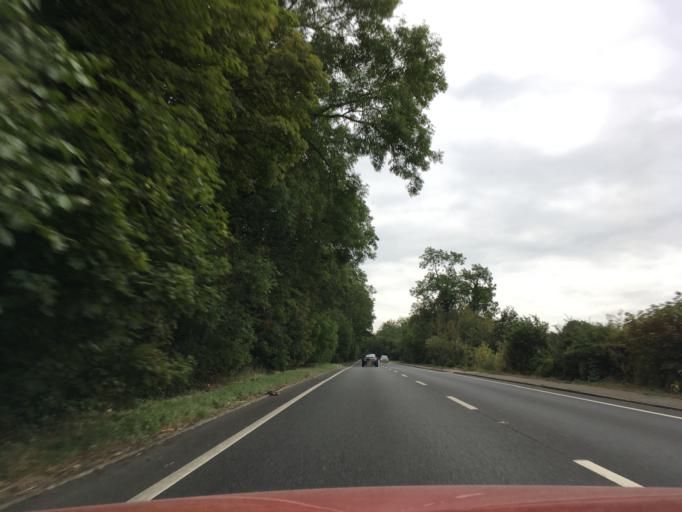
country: GB
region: England
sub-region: Central Bedfordshire
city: Battlesden
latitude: 51.9410
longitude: -0.6027
